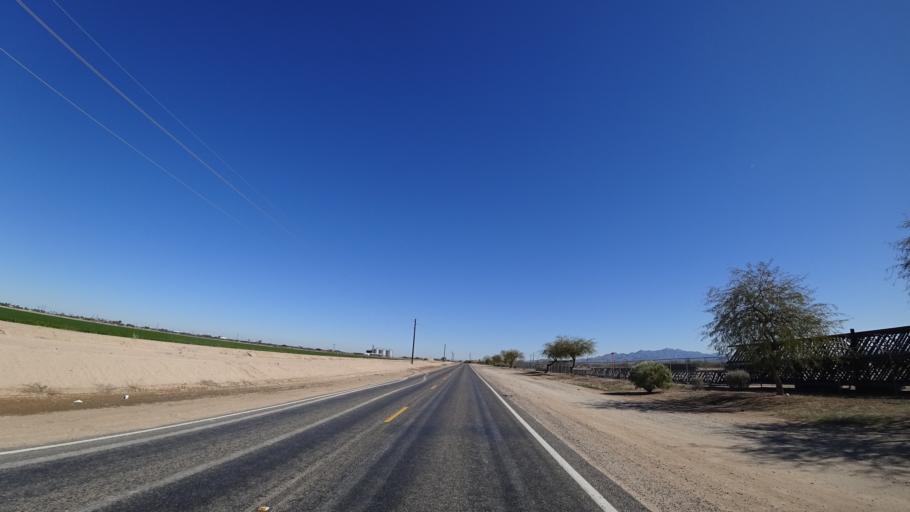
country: US
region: Arizona
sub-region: Maricopa County
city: Buckeye
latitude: 33.3922
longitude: -112.5253
